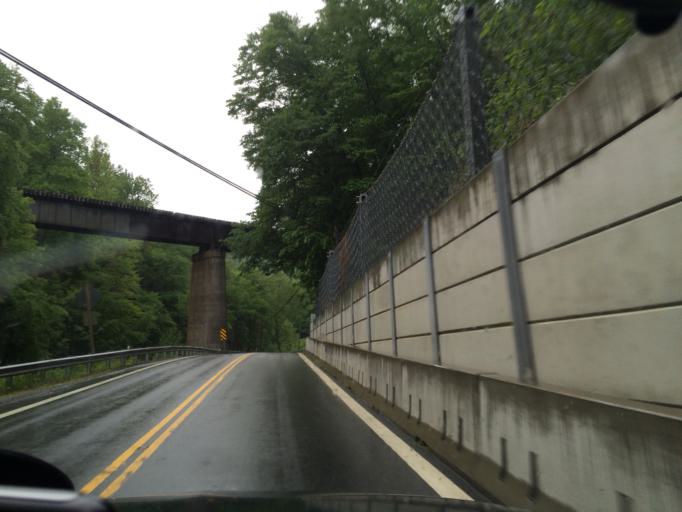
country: US
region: Maryland
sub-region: Frederick County
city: Thurmont
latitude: 39.6510
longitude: -77.4234
